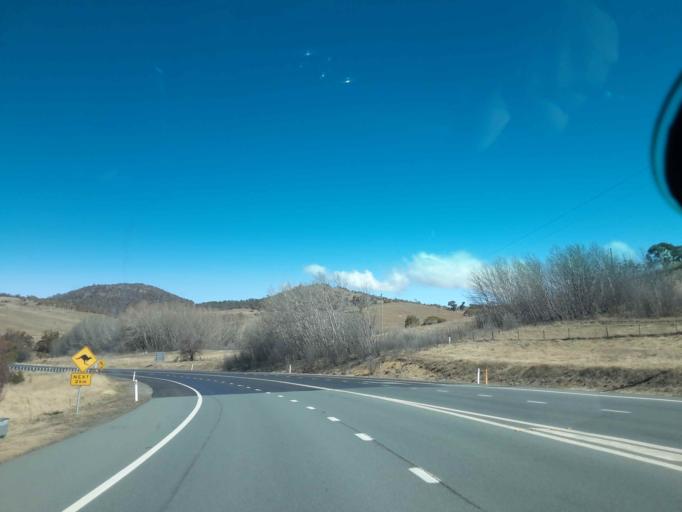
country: AU
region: New South Wales
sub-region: Snowy River
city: Jindabyne
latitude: -36.4112
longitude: 148.5950
